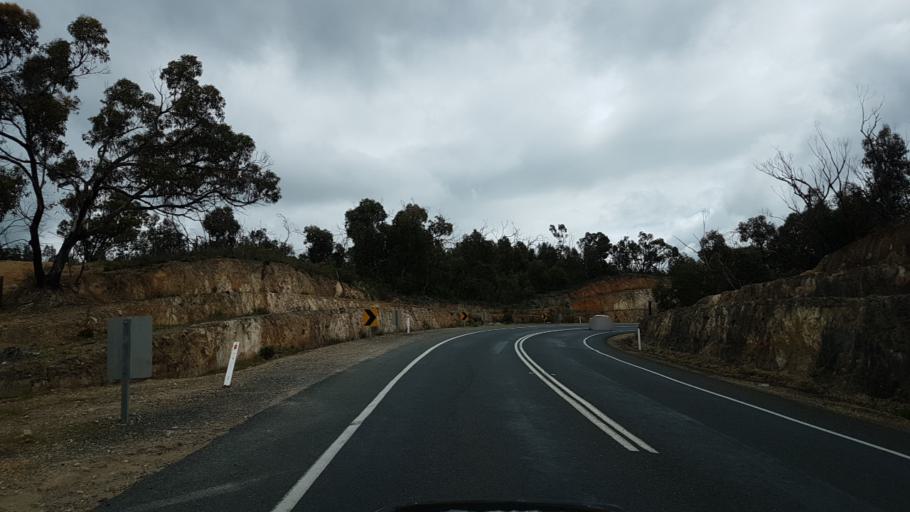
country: AU
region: South Australia
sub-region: Playford
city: One Tree Hill
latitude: -34.7644
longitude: 138.8162
